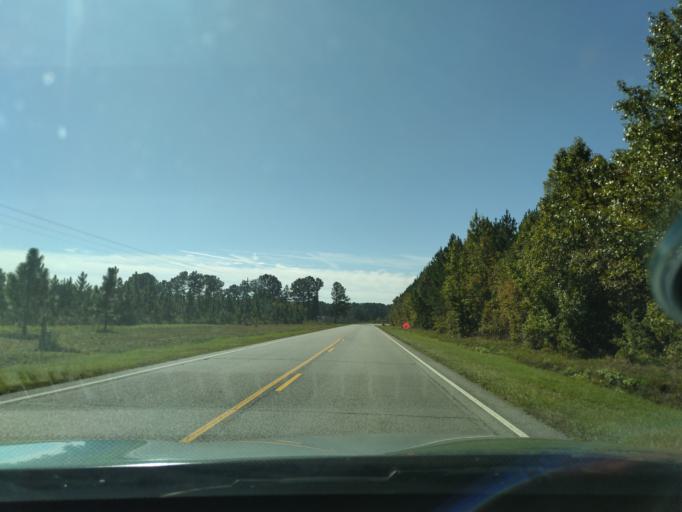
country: US
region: North Carolina
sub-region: Beaufort County
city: Belhaven
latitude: 35.6357
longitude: -76.8049
